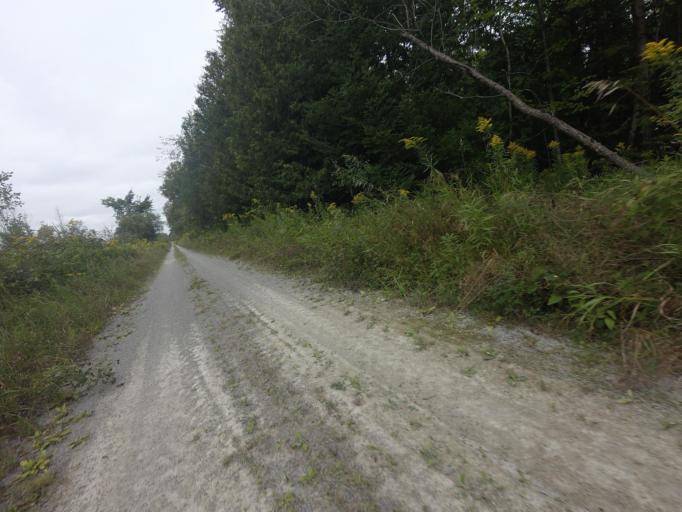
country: CA
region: Ontario
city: Uxbridge
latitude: 44.2775
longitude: -79.0095
